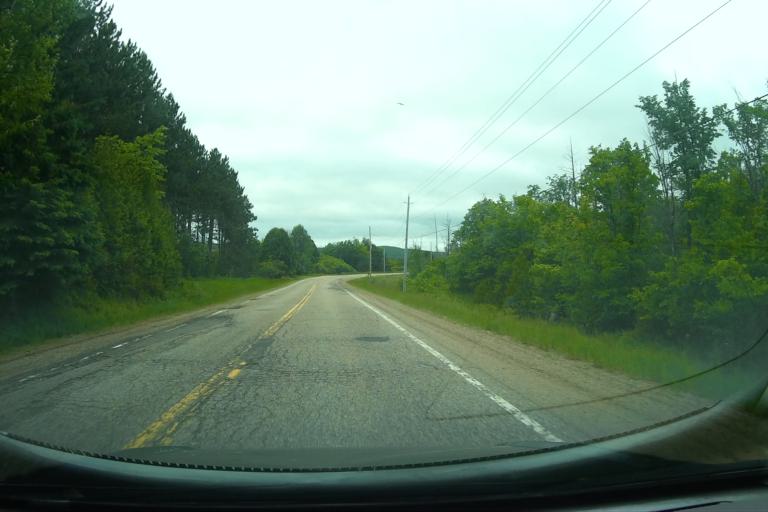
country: CA
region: Ontario
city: Pembroke
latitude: 45.4608
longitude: -77.2547
